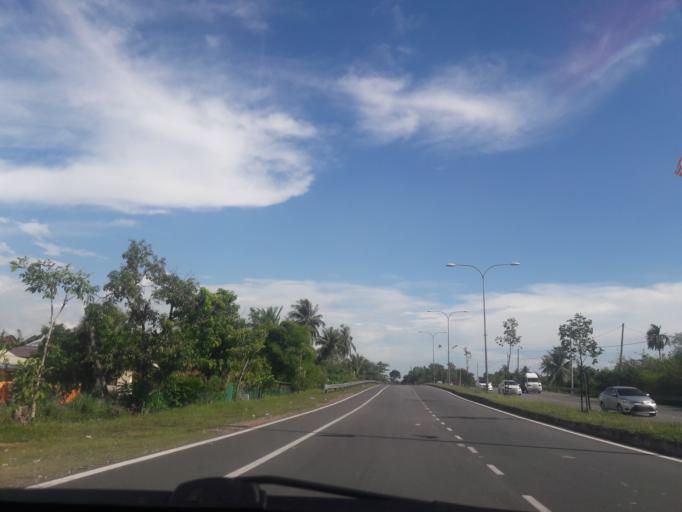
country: MY
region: Kedah
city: Sungai Petani
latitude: 5.6231
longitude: 100.4642
